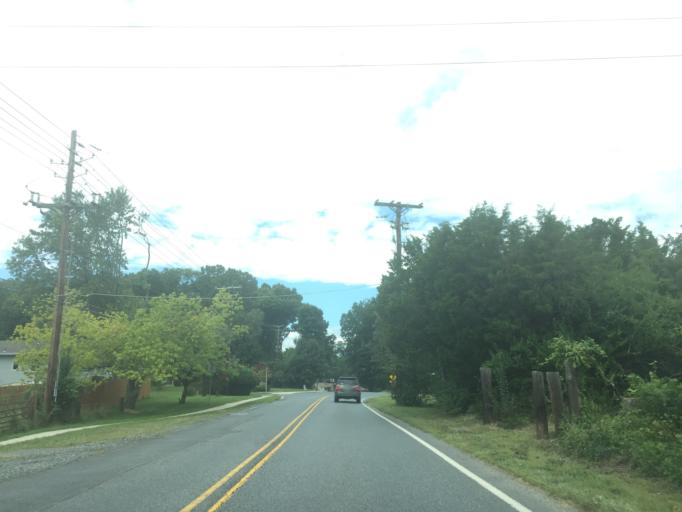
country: US
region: Maryland
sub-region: Montgomery County
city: Gaithersburg
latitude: 39.1313
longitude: -77.2446
